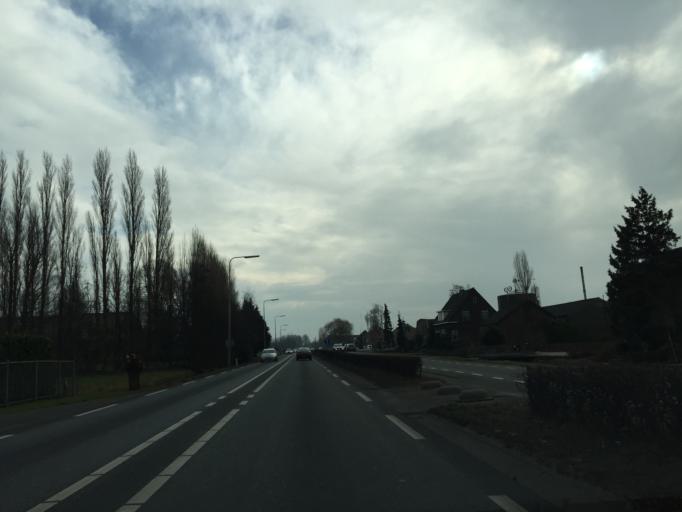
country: NL
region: South Holland
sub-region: Gemeente Capelle aan den IJssel
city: Capelle aan den IJssel
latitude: 51.9869
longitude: 4.6040
